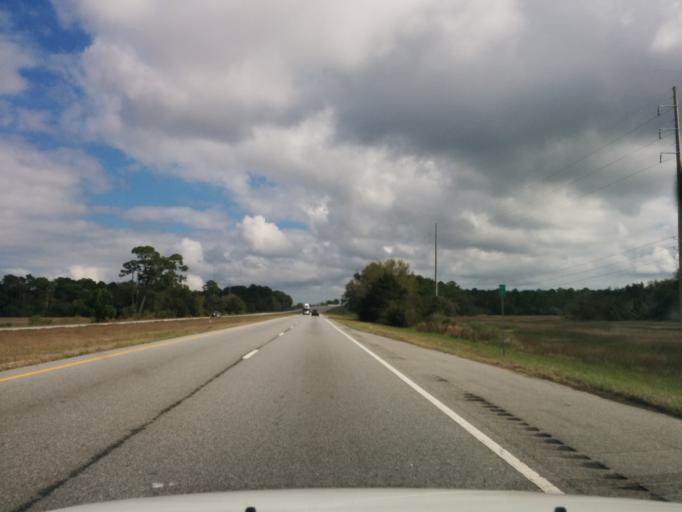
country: US
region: Georgia
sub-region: Glynn County
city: Brunswick
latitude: 31.1251
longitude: -81.5494
